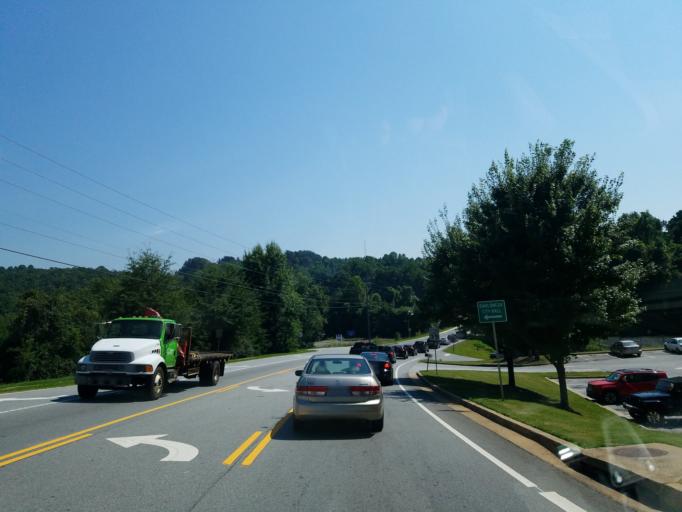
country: US
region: Georgia
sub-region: Lumpkin County
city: Dahlonega
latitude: 34.5305
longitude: -83.9777
